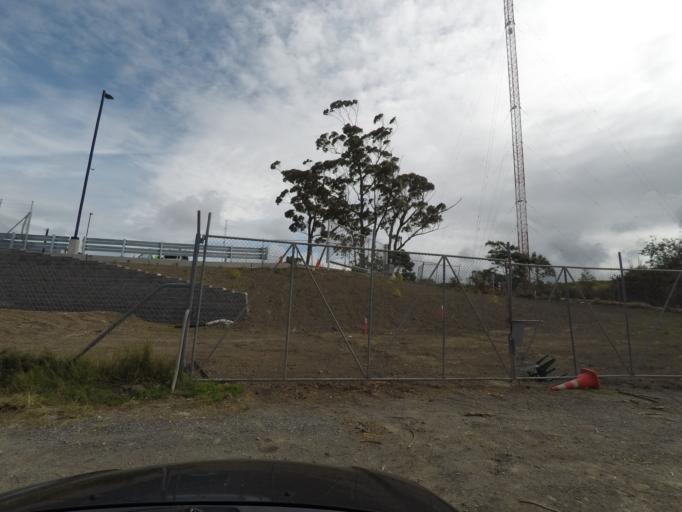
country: NZ
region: Auckland
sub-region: Auckland
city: Rosebank
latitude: -36.8440
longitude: 174.6325
